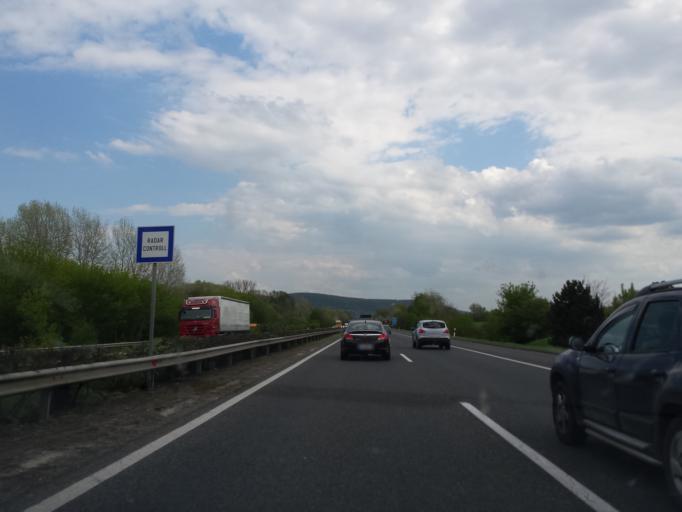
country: HU
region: Komarom-Esztergom
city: Vertesszolos
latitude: 47.6151
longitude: 18.3471
